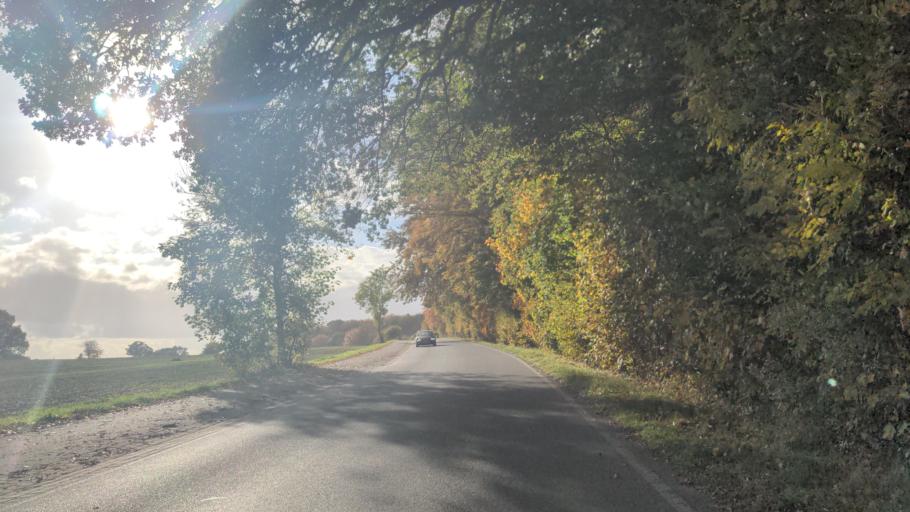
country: DE
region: Schleswig-Holstein
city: Bosdorf
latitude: 54.1324
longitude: 10.4734
